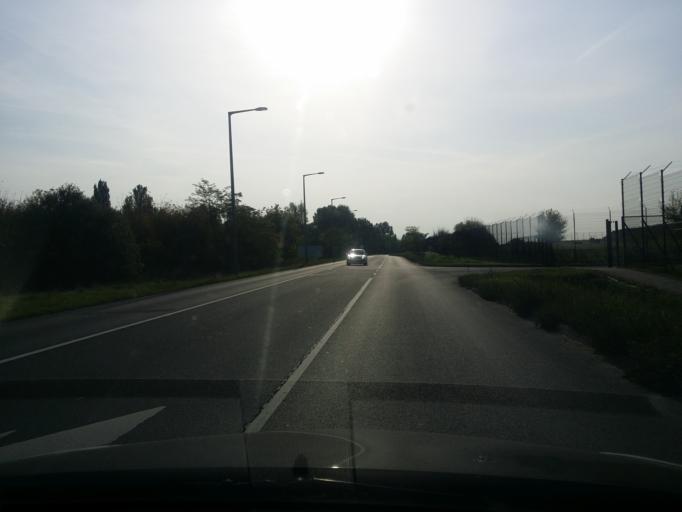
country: HU
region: Budapest
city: Budapest XV. keruelet
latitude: 47.5815
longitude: 19.1382
